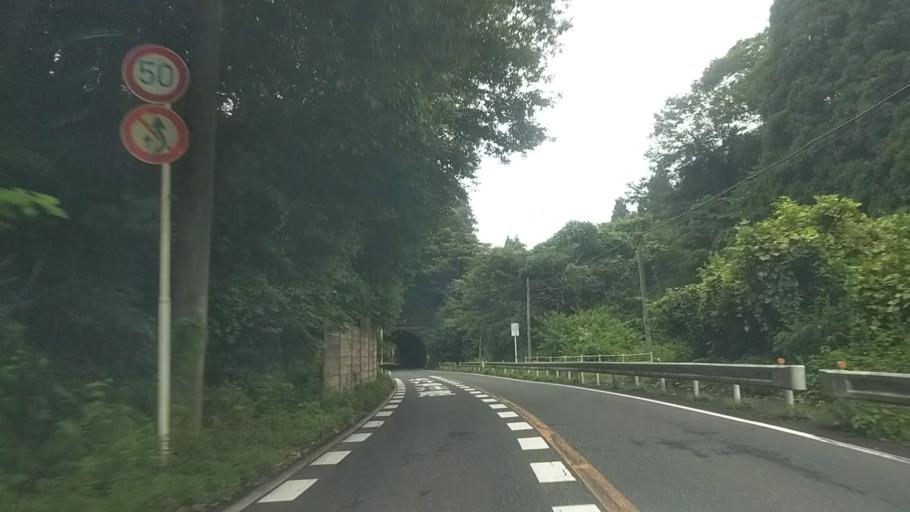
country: JP
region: Chiba
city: Kawaguchi
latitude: 35.2543
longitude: 140.0660
